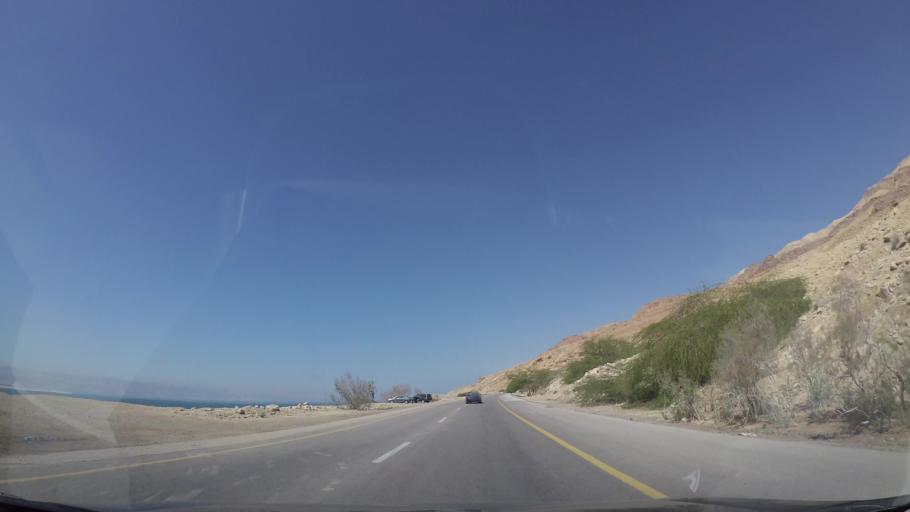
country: JO
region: Karak
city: Al Qasr
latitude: 31.3550
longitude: 35.5479
